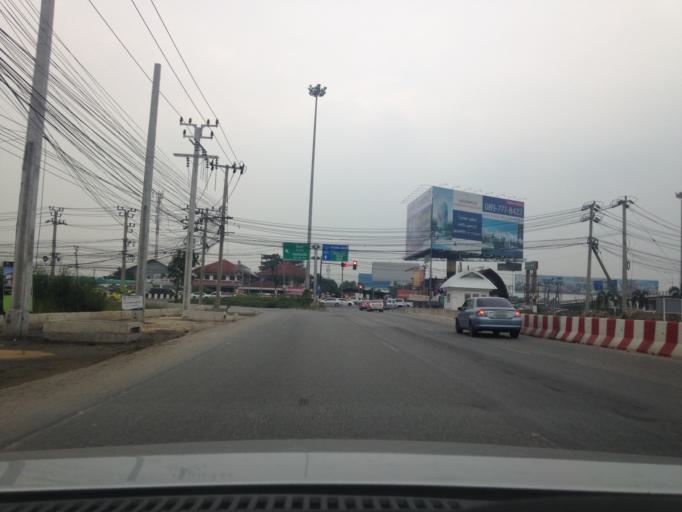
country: TH
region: Bangkok
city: Lat Krabang
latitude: 13.7308
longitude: 100.7455
